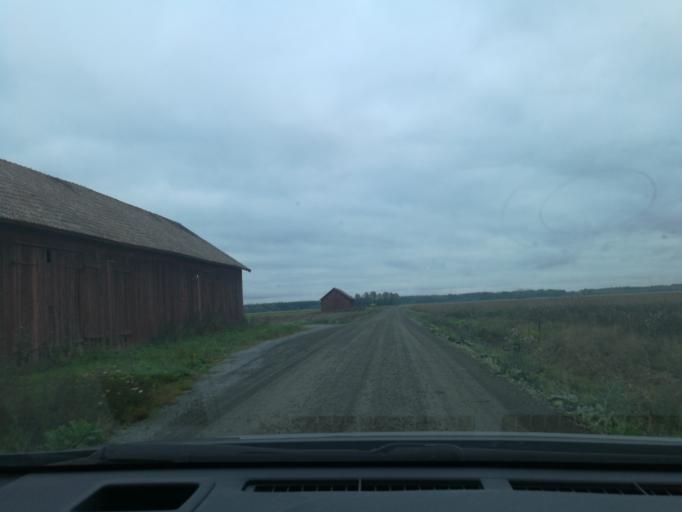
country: SE
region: Vaestmanland
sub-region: Vasteras
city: Tillberga
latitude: 59.7697
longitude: 16.6533
